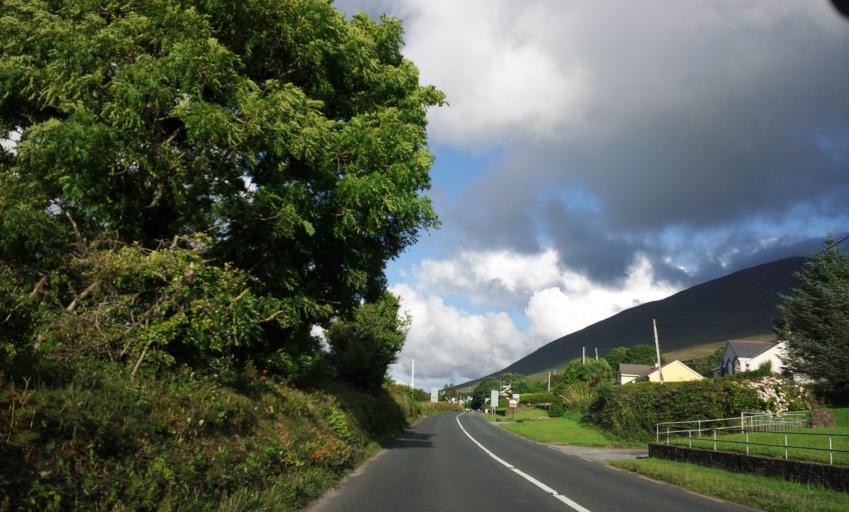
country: IE
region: Munster
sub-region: Ciarrai
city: Killorglin
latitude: 52.2260
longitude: -9.8983
